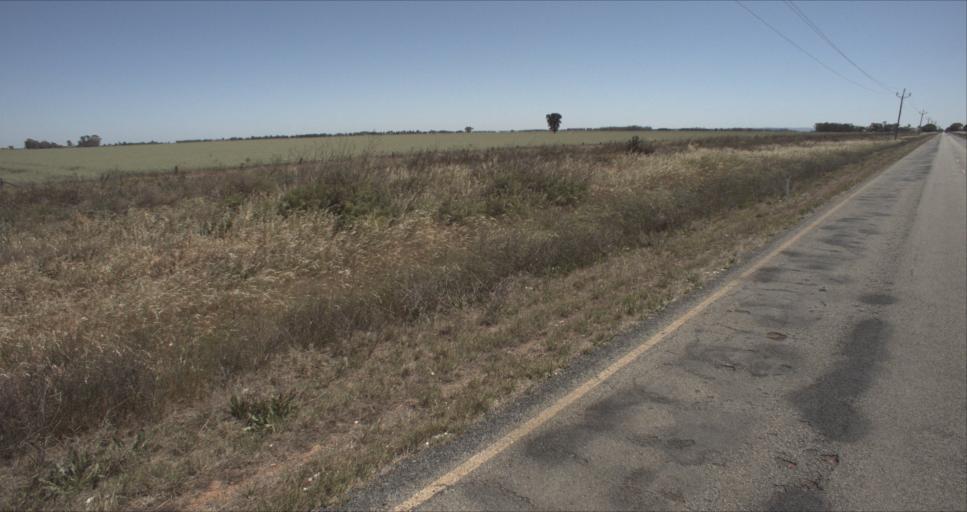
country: AU
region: New South Wales
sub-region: Leeton
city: Leeton
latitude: -34.5117
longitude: 146.2850
